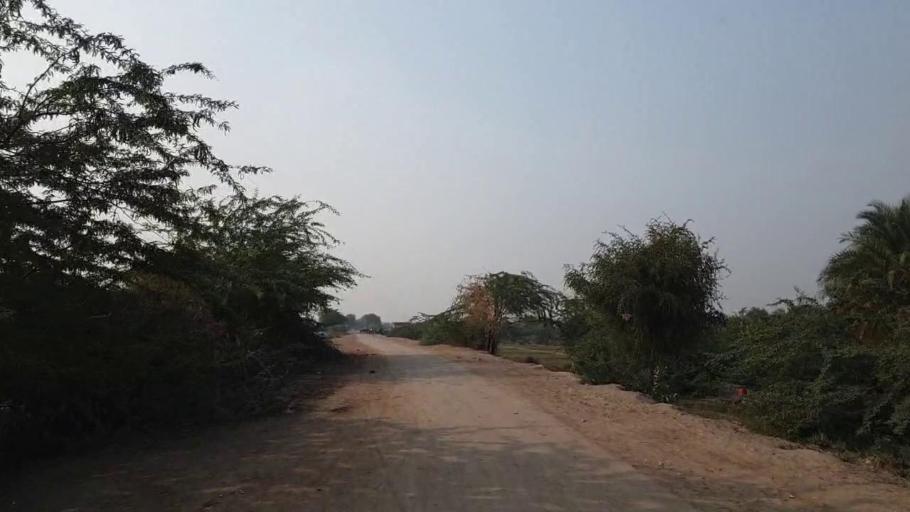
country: PK
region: Sindh
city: Bhan
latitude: 26.5590
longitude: 67.7101
